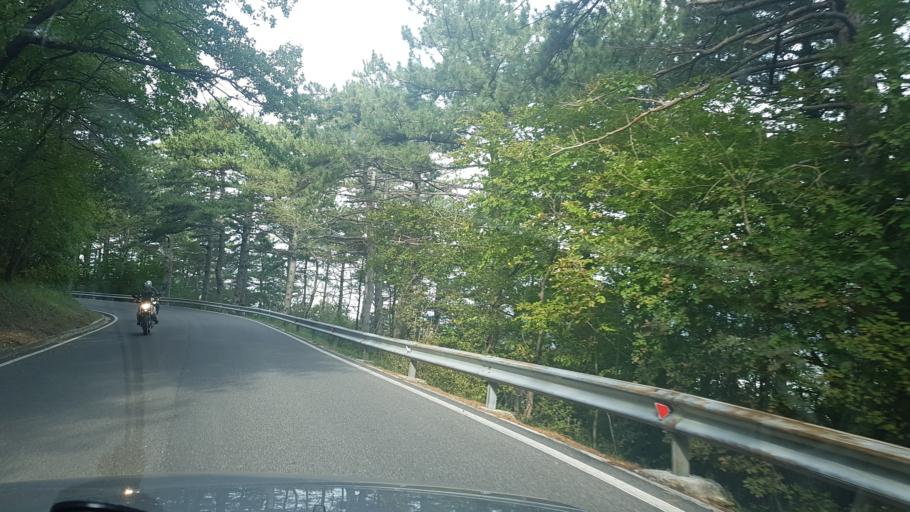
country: IT
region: Friuli Venezia Giulia
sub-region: Provincia di Trieste
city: Dolina
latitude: 45.5951
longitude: 13.8559
